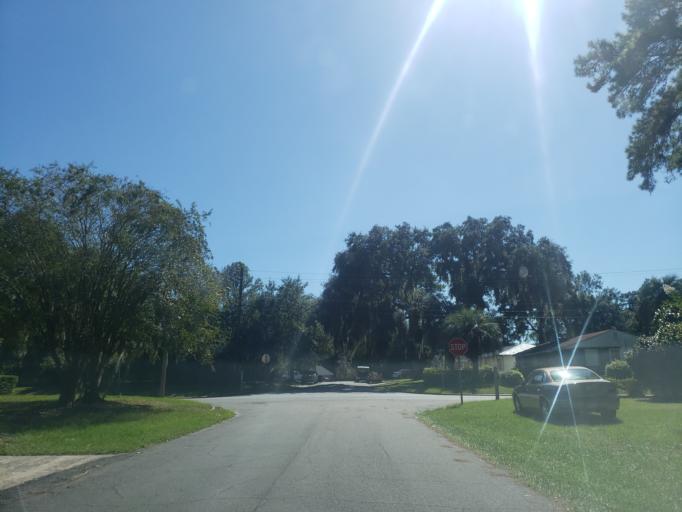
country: US
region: Georgia
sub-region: Chatham County
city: Thunderbolt
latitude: 32.0366
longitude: -81.0738
